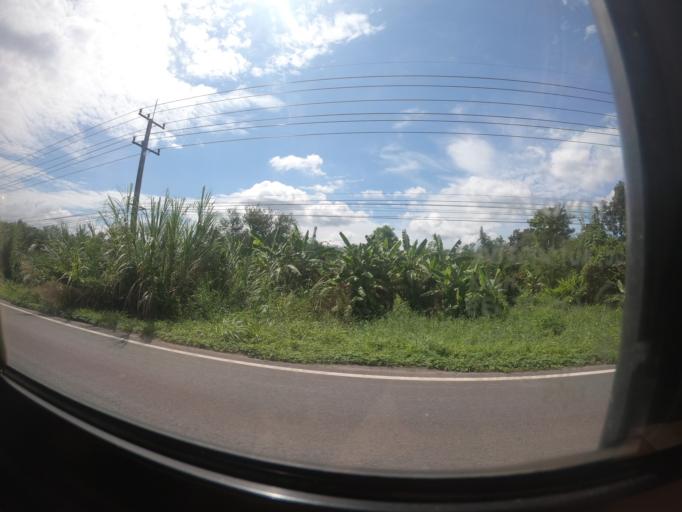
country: TH
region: Nakhon Nayok
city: Nakhon Nayok
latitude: 14.2906
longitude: 101.3036
